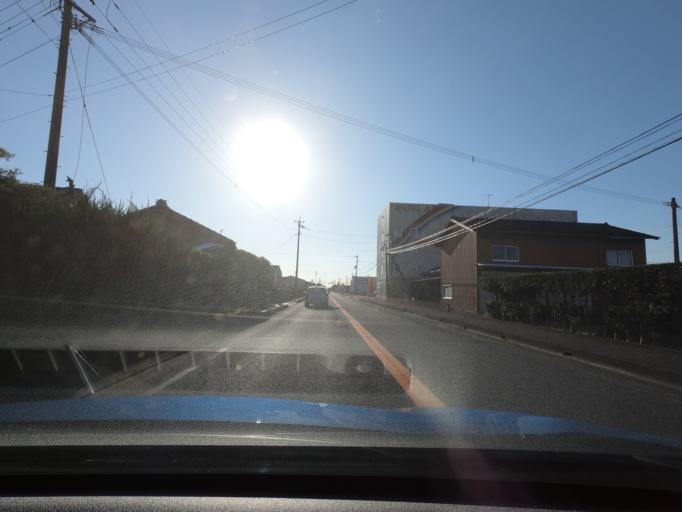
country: JP
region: Kagoshima
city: Izumi
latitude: 32.0981
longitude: 130.3042
